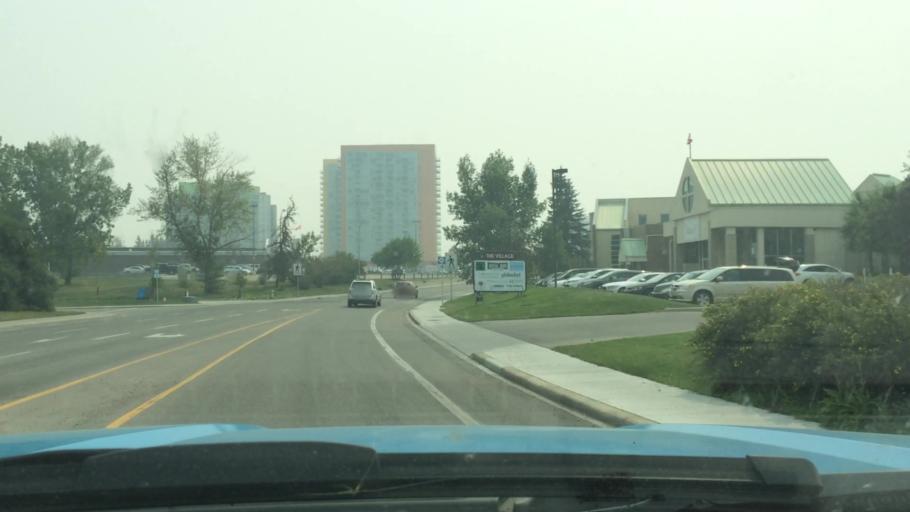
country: CA
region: Alberta
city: Calgary
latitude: 51.0894
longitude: -114.1333
